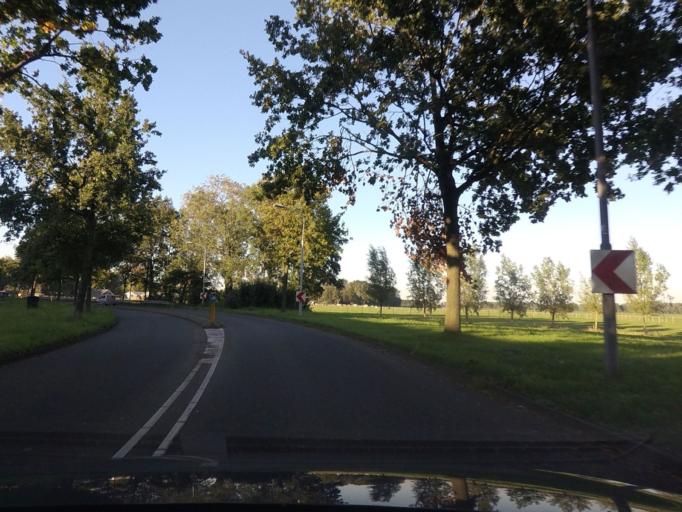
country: NL
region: North Holland
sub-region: Gemeente Bloemendaal
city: Bloemendaal
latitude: 52.4178
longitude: 4.6596
